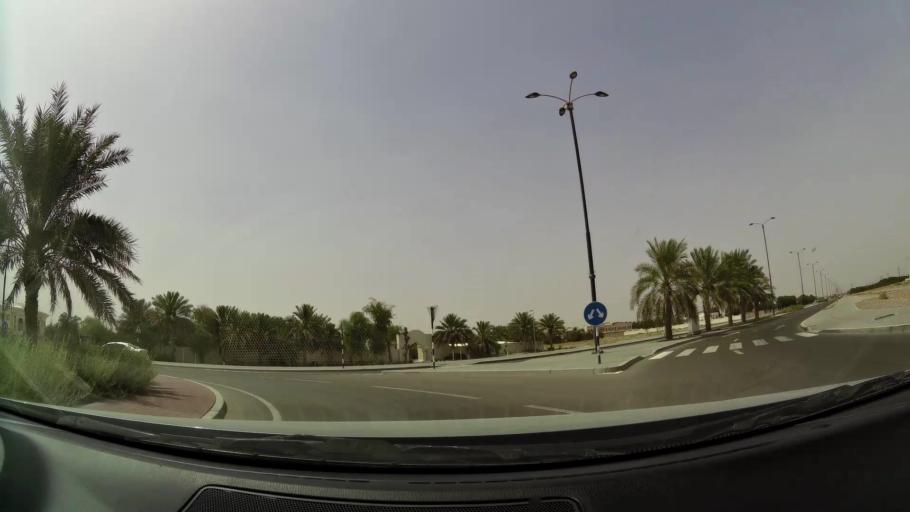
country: AE
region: Abu Dhabi
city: Al Ain
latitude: 24.1508
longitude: 55.6568
